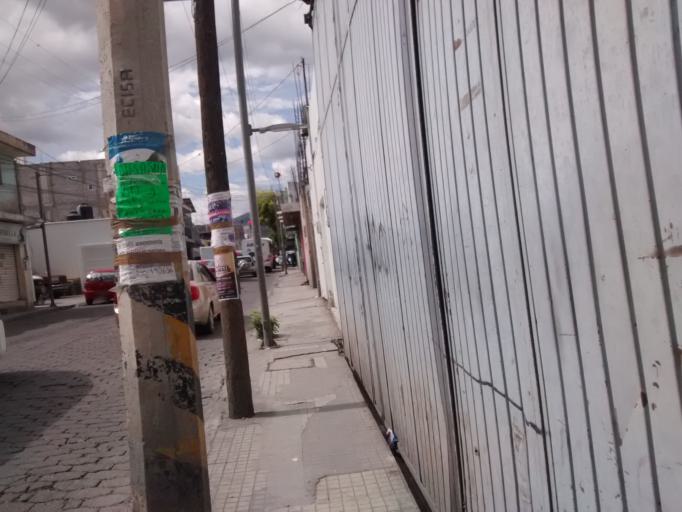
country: MX
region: Puebla
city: Tehuacan
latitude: 18.4599
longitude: -97.3871
